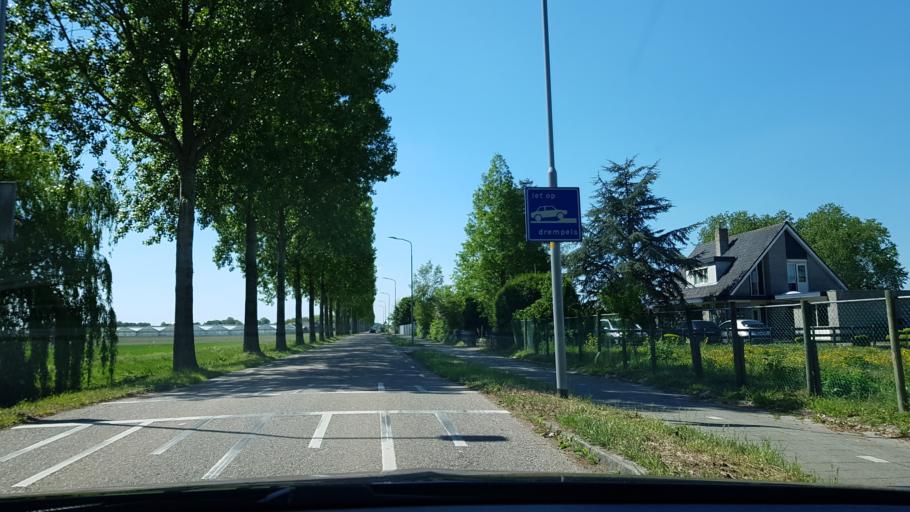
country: NL
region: South Holland
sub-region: Gemeente Kaag en Braassem
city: Leimuiden
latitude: 52.2478
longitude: 4.6890
